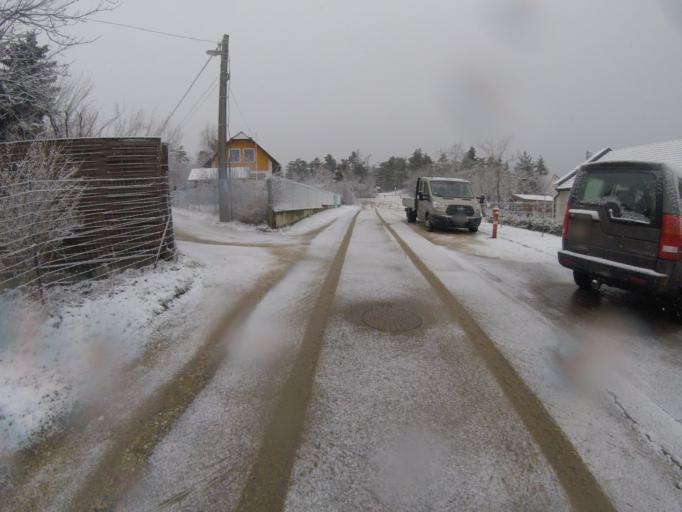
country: HU
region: Pest
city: Pilisszentivan
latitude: 47.5888
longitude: 18.8963
